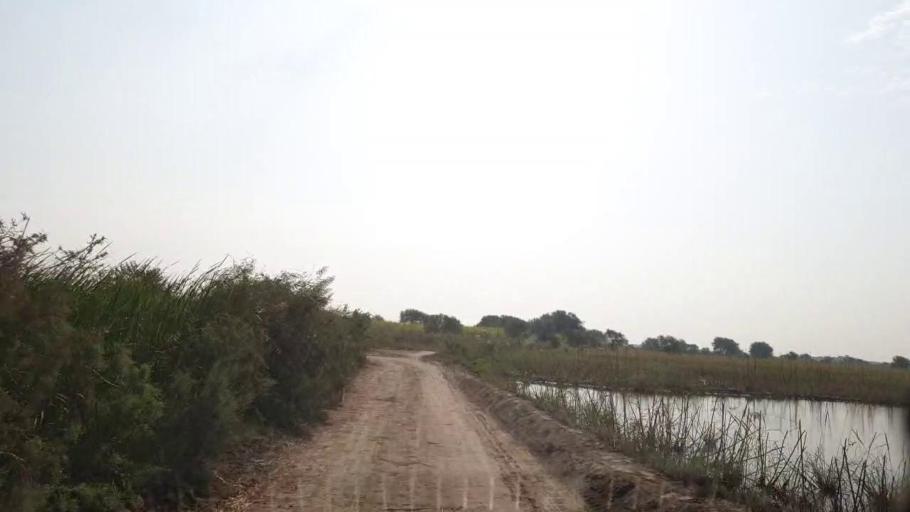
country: PK
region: Sindh
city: Tando Muhammad Khan
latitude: 25.0603
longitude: 68.4271
